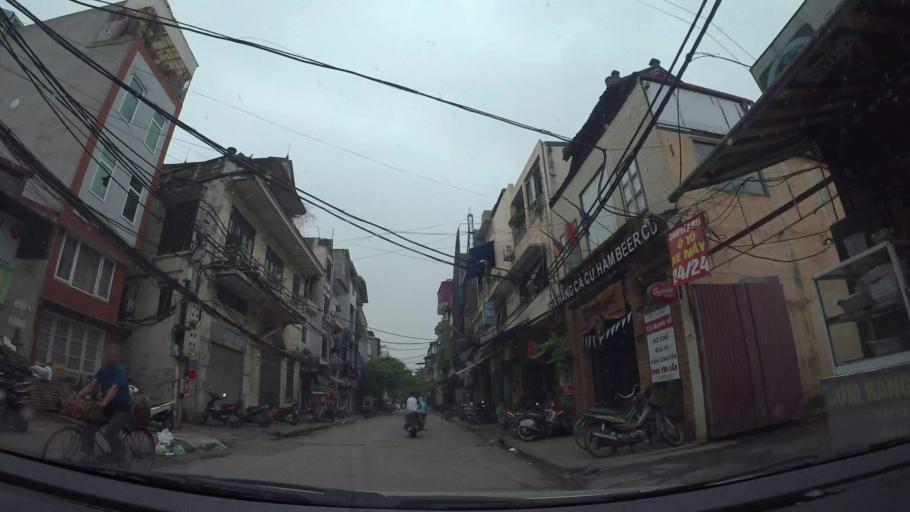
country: VN
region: Ha Noi
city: Hoan Kiem
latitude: 21.0523
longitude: 105.8406
